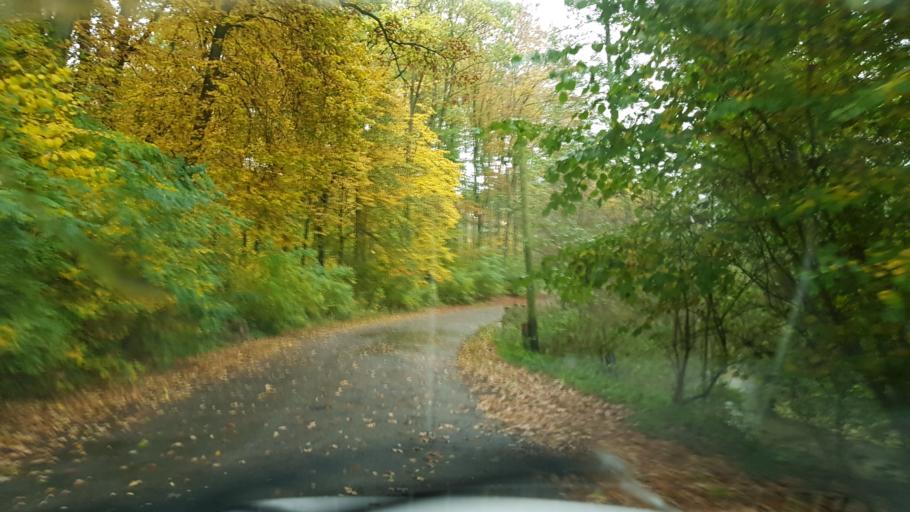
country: PL
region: West Pomeranian Voivodeship
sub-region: Powiat mysliborski
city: Barlinek
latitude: 53.0138
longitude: 15.2237
